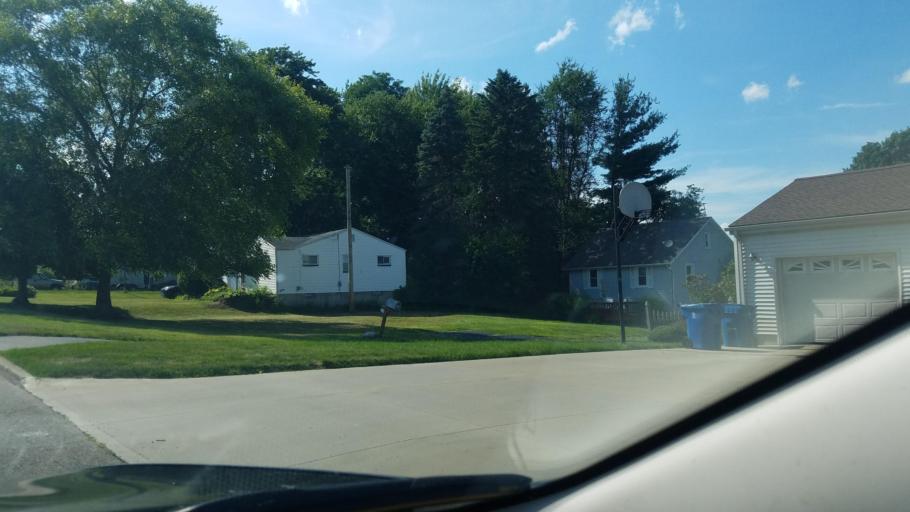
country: US
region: Ohio
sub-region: Mahoning County
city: Struthers
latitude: 41.0463
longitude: -80.6117
